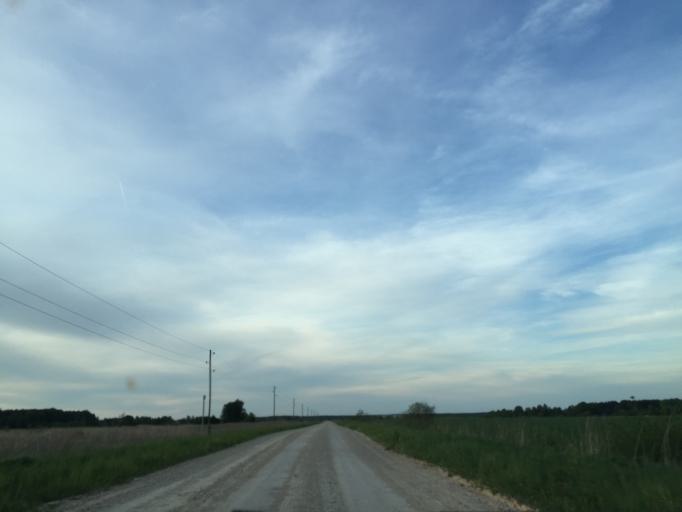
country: LV
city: Tireli
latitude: 56.7948
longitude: 23.5659
